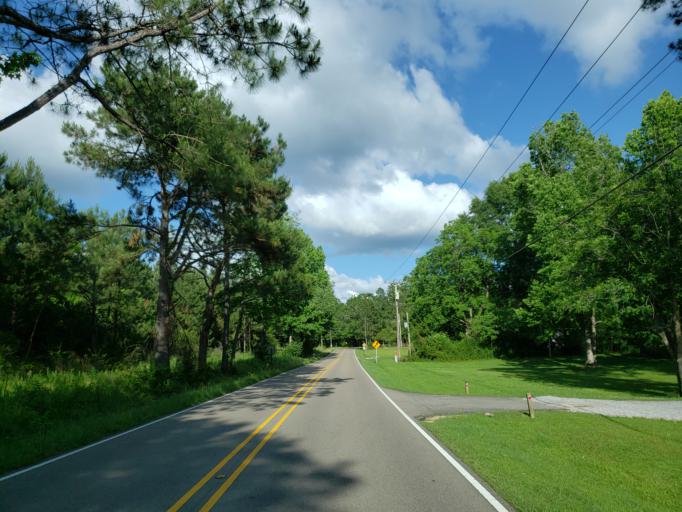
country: US
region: Mississippi
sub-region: Lamar County
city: West Hattiesburg
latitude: 31.2737
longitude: -89.3669
